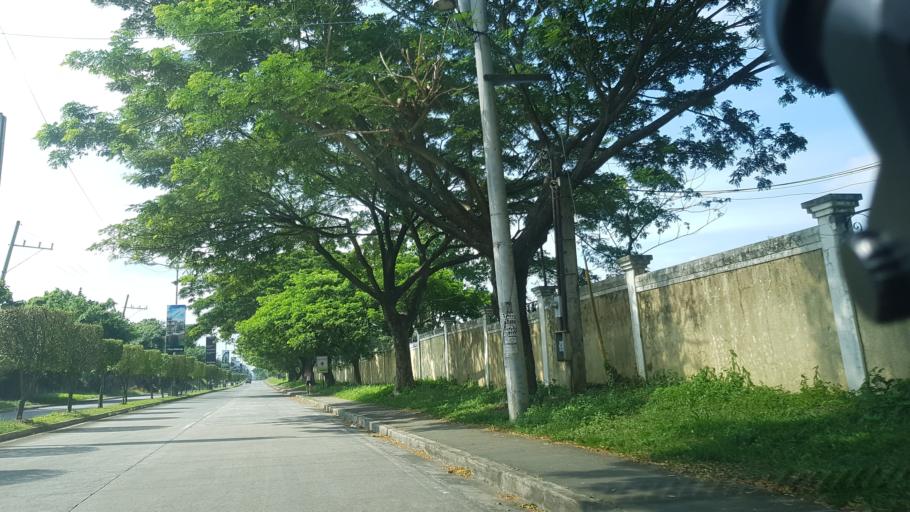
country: PH
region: Calabarzon
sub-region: Province of Laguna
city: Magsaysay
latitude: 14.3668
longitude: 121.0098
